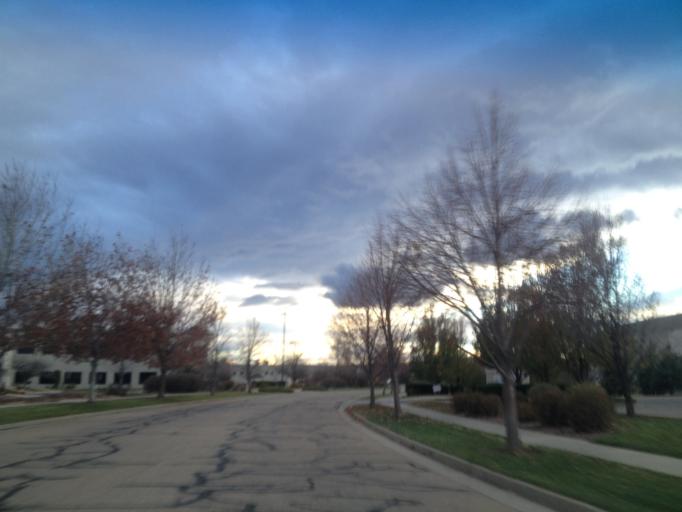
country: US
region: Colorado
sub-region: Boulder County
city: Louisville
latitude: 39.9691
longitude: -105.1125
